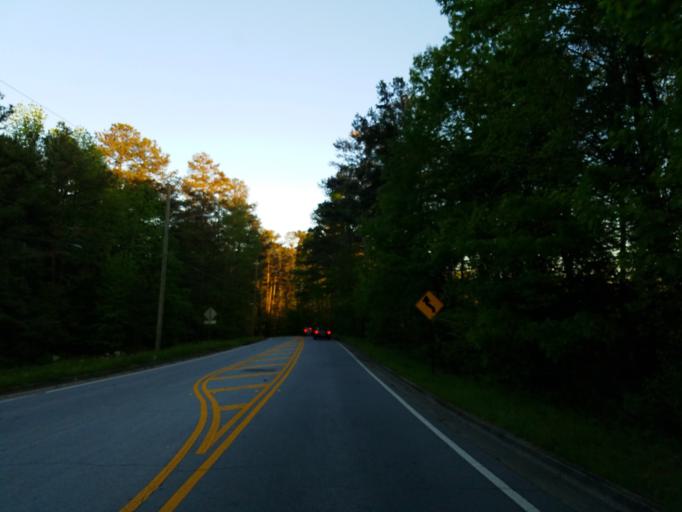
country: US
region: Georgia
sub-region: Cobb County
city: Fair Oaks
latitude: 33.8872
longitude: -84.5841
